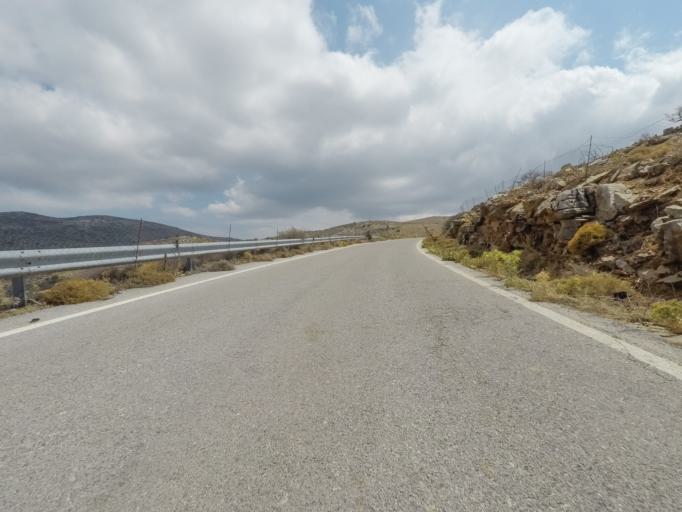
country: GR
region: Crete
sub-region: Nomos Lasithiou
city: Elounda
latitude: 35.3120
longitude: 25.6804
